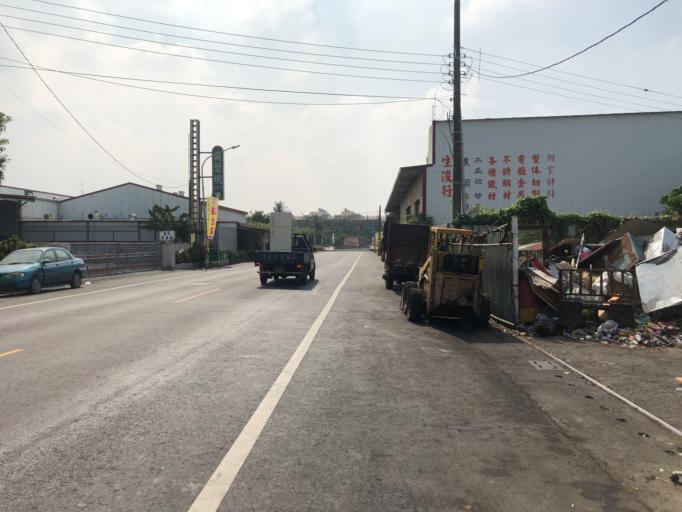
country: TW
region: Taiwan
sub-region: Pingtung
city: Pingtung
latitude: 22.5485
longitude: 120.5339
